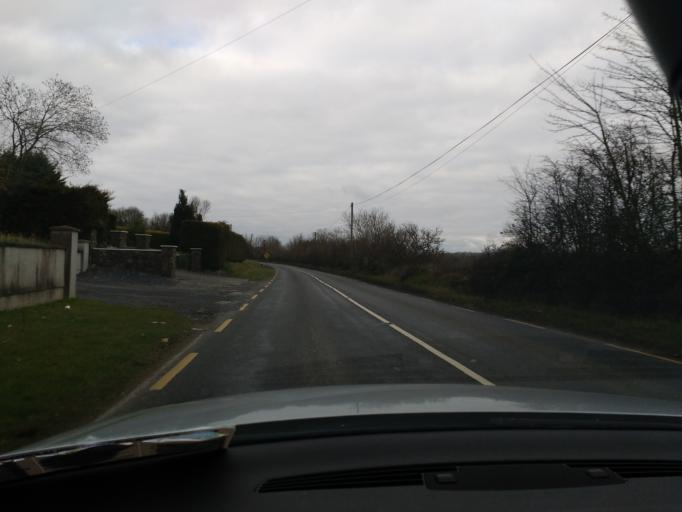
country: IE
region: Leinster
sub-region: Kilkenny
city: Kilkenny
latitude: 52.6870
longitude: -7.2754
